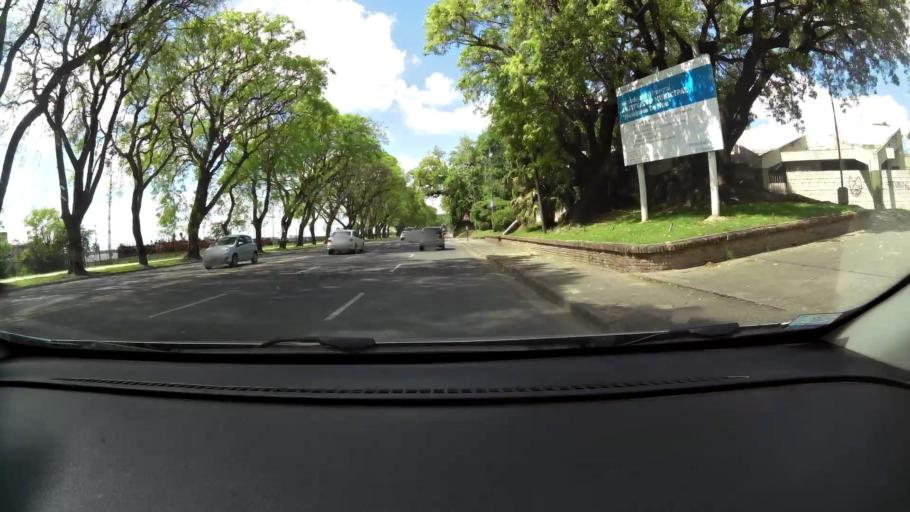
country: AR
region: Santa Fe
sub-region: Departamento de Rosario
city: Rosario
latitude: -32.9577
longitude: -60.6221
